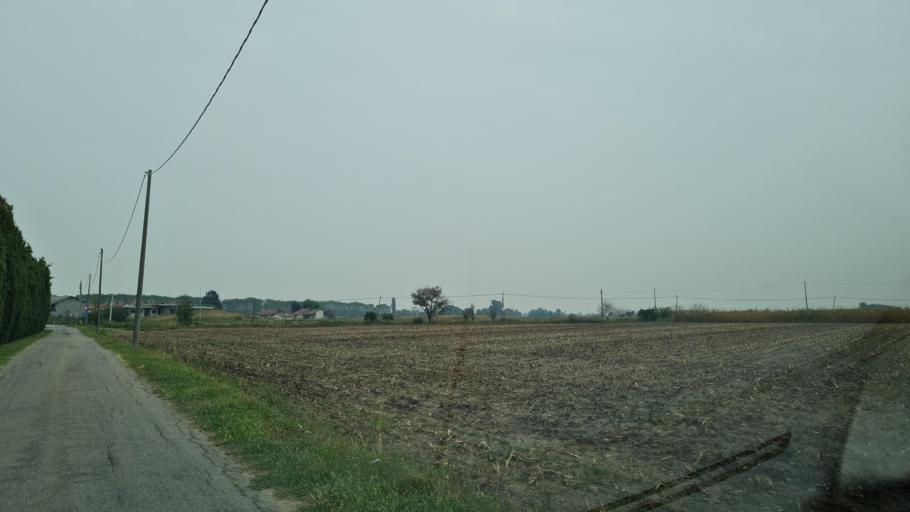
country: IT
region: Piedmont
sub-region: Provincia di Novara
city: Mandello Vitta
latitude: 45.4928
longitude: 8.4557
